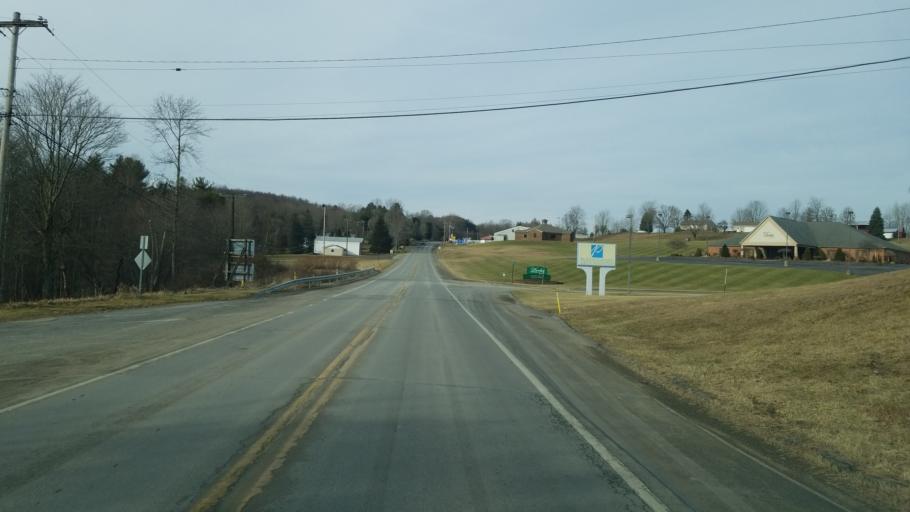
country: US
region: Pennsylvania
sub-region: Jefferson County
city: Punxsutawney
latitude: 40.9592
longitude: -79.0036
